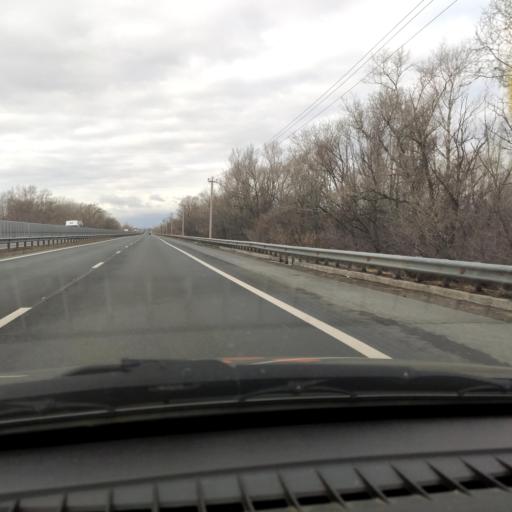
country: RU
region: Samara
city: Novosemeykino
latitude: 53.4250
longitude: 50.3173
